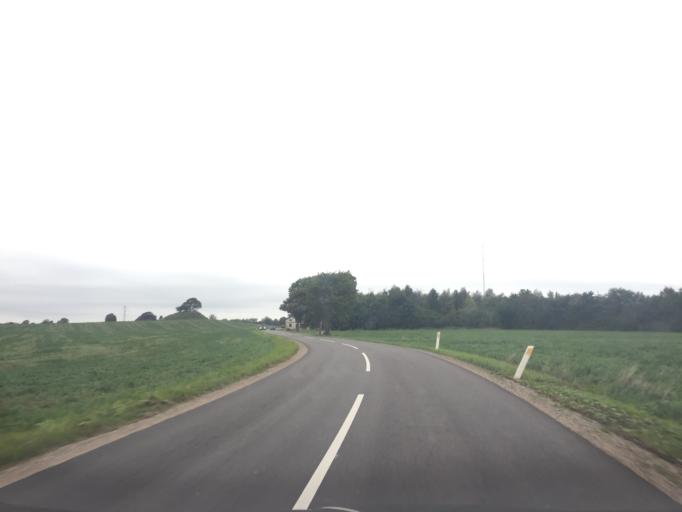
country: DK
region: Capital Region
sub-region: Egedal Kommune
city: Vekso
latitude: 55.6992
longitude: 12.2306
